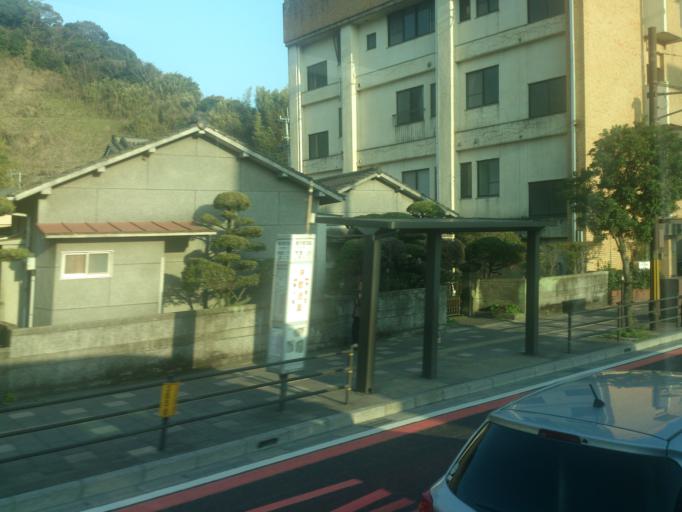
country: JP
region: Kagoshima
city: Kagoshima-shi
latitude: 31.6194
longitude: 130.5267
